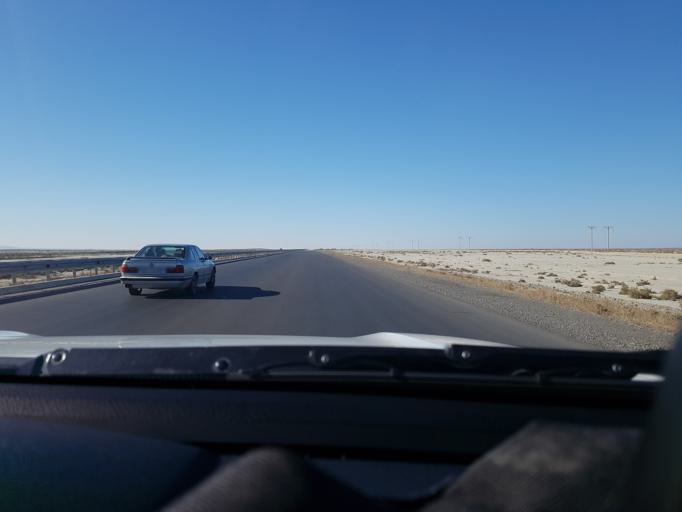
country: TM
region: Balkan
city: Gazanjyk
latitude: 39.2536
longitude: 55.1034
